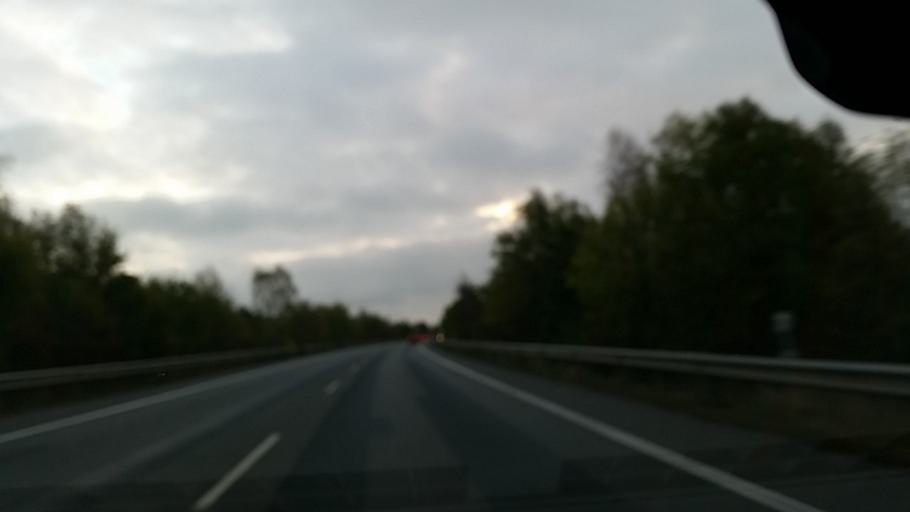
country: DE
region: Lower Saxony
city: Tappenbeck
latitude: 52.4610
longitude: 10.7465
